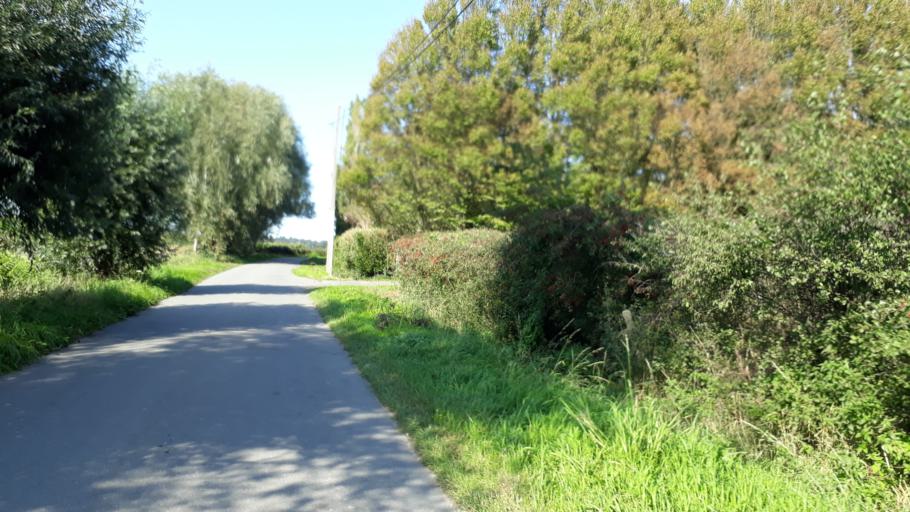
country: BE
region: Flanders
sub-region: Provincie West-Vlaanderen
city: Kortemark
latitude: 51.0524
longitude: 3.0567
